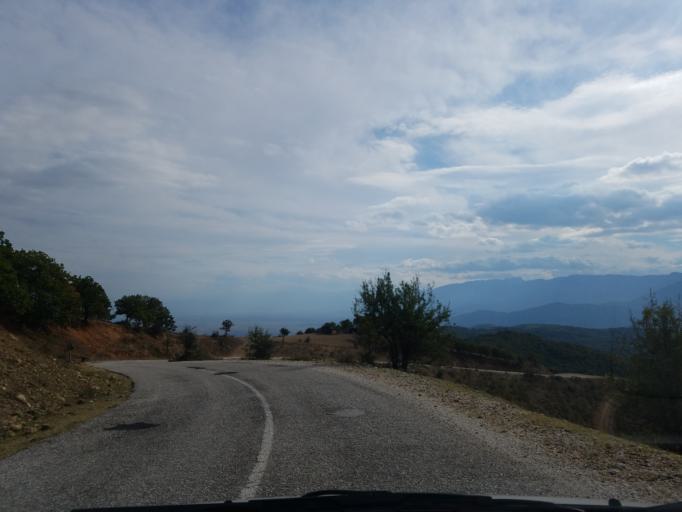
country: GR
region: Thessaly
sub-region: Trikala
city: Kastraki
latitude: 39.7506
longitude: 21.6613
